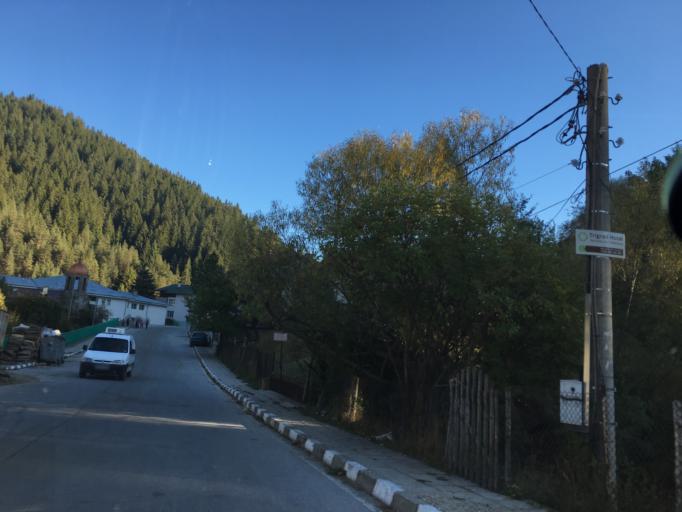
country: BG
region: Smolyan
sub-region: Obshtina Borino
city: Borino
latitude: 41.5981
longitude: 24.3789
